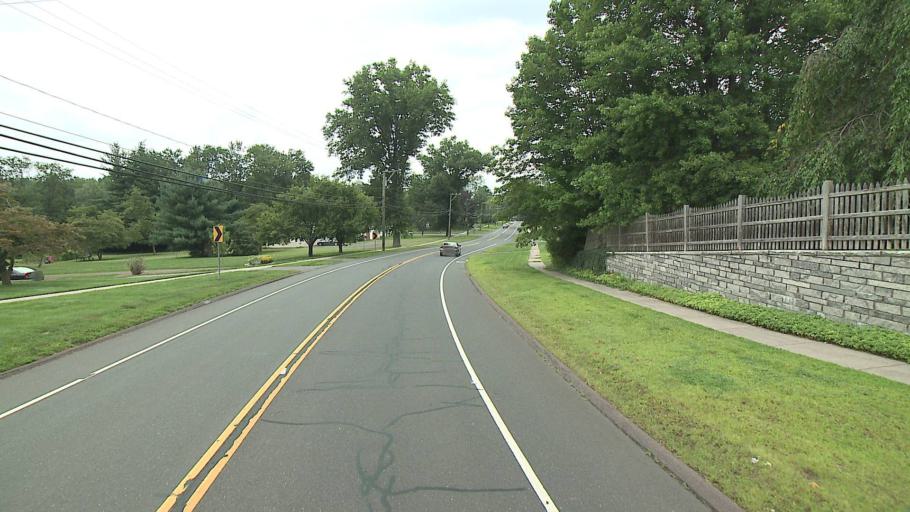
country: US
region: Connecticut
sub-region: Hartford County
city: Wethersfield
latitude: 41.6859
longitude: -72.6638
